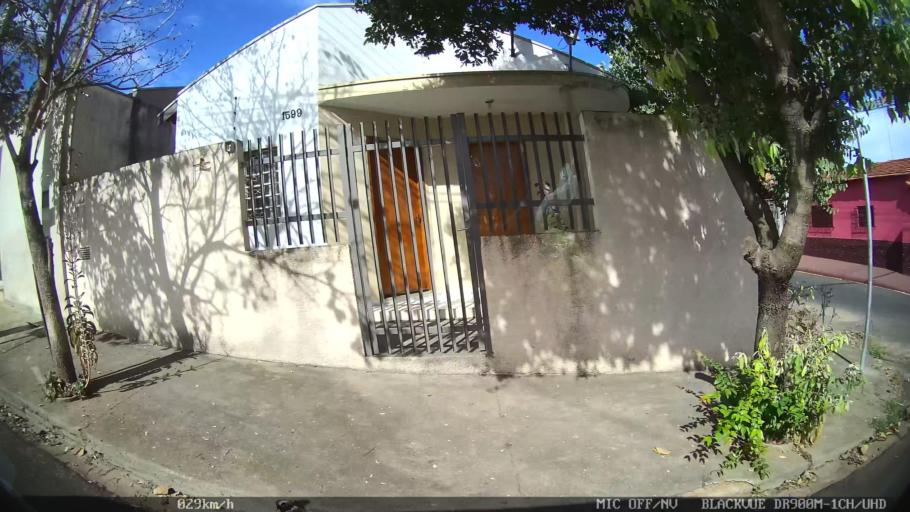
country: BR
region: Sao Paulo
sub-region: Catanduva
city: Catanduva
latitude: -21.1257
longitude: -48.9760
